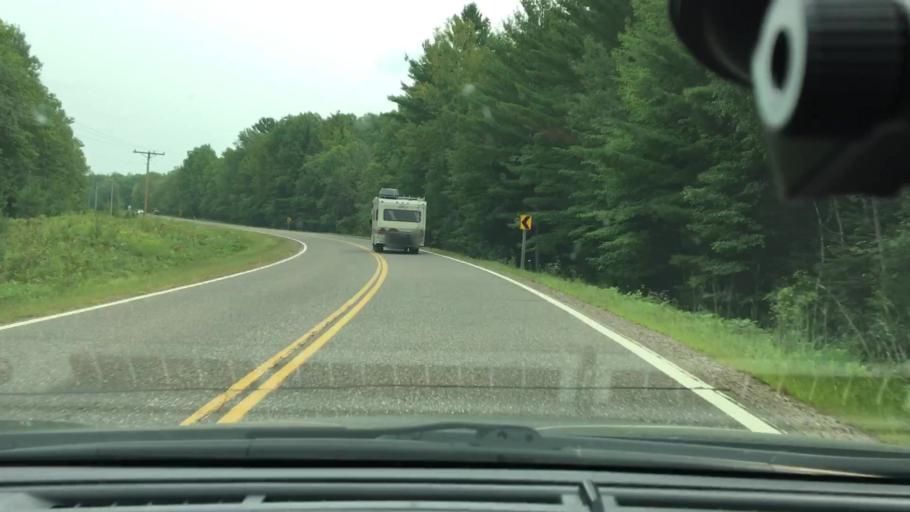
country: US
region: Minnesota
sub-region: Aitkin County
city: Aitkin
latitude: 46.4019
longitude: -93.8004
